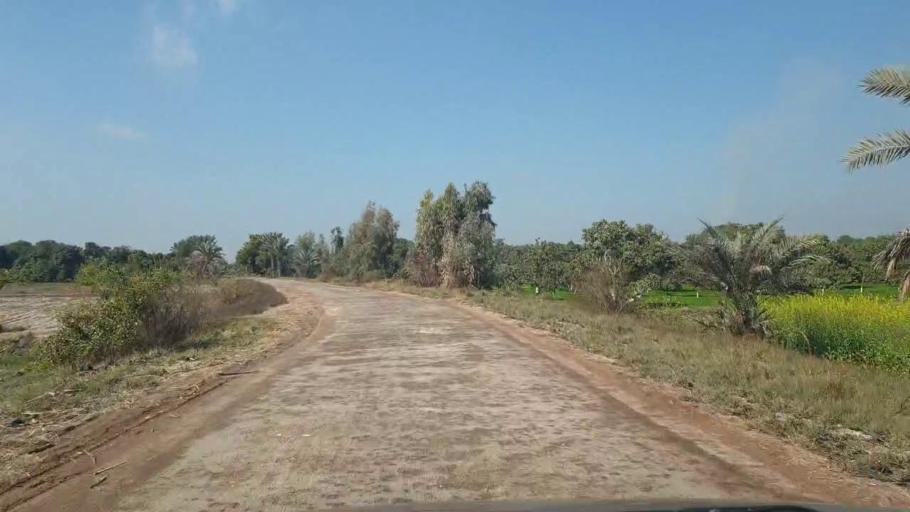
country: PK
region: Sindh
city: Shahdadpur
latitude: 25.9130
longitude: 68.5922
